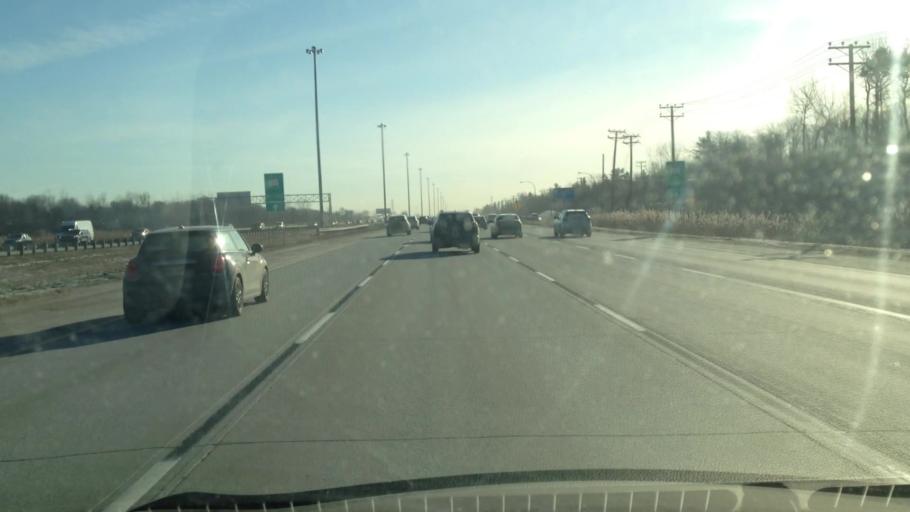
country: CA
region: Quebec
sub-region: Laurentides
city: Blainville
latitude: 45.6552
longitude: -73.8814
